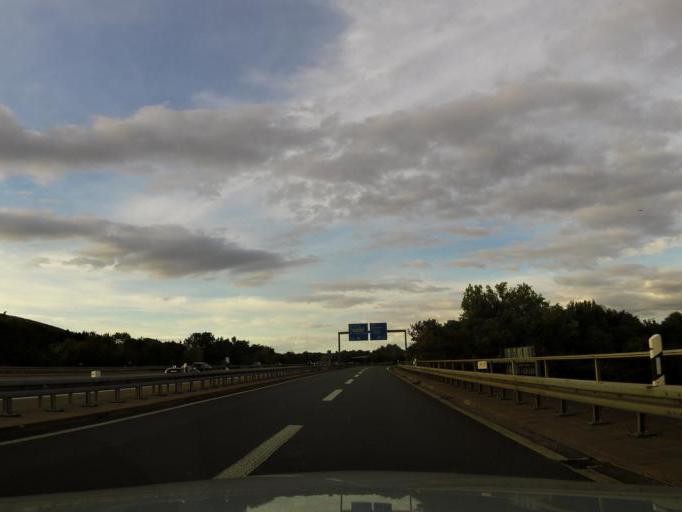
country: DE
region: Hesse
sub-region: Regierungsbezirk Darmstadt
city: Neu Isenburg
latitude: 50.0642
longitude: 8.7270
